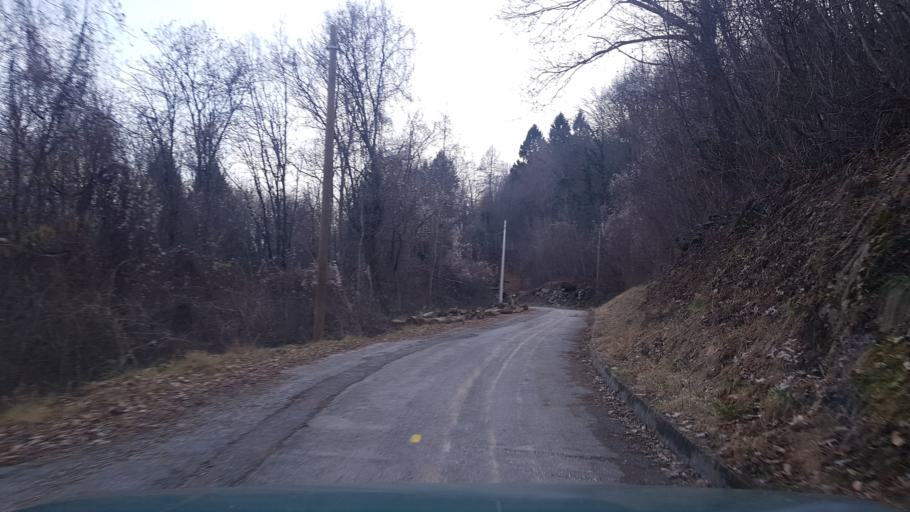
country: IT
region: Friuli Venezia Giulia
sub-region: Provincia di Udine
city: Pulfero
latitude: 46.1449
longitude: 13.4620
